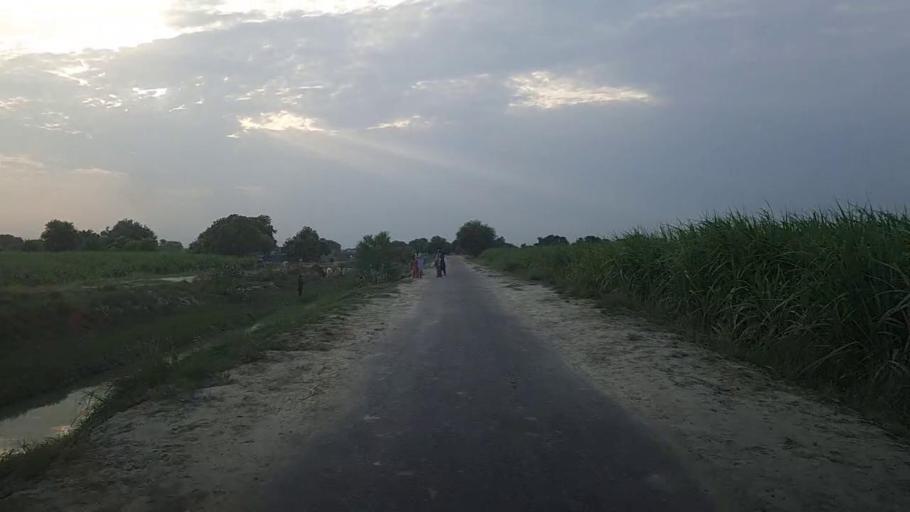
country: PK
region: Sindh
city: Ubauro
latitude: 28.3587
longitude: 69.7867
